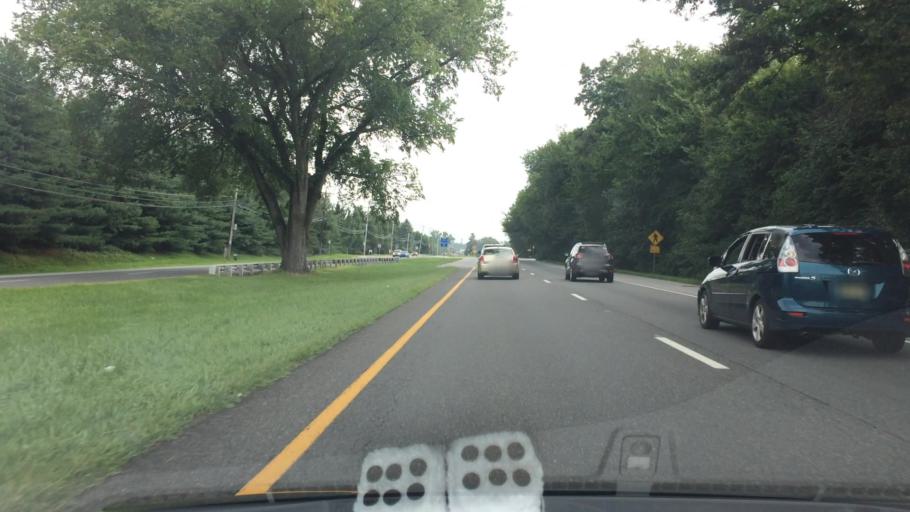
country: US
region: Delaware
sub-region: New Castle County
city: Bear
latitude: 39.6370
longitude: -75.6299
